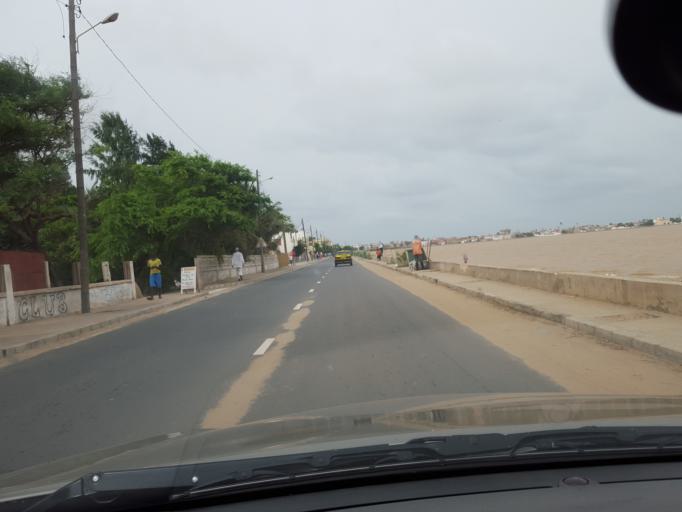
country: SN
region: Saint-Louis
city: Saint-Louis
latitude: 16.0322
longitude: -16.4907
